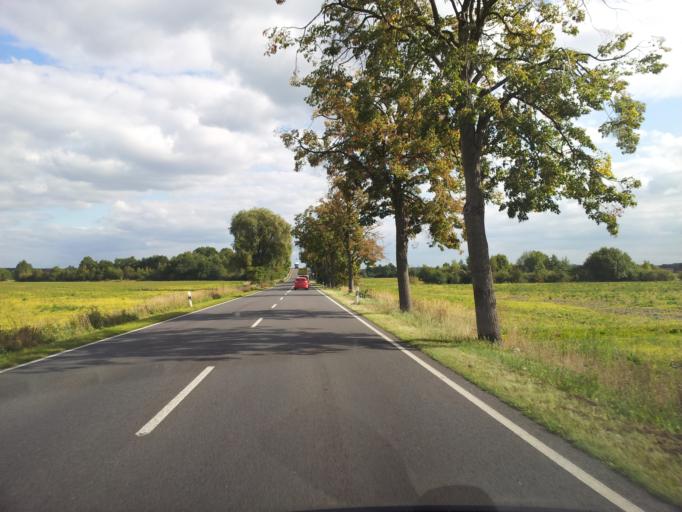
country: DE
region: Brandenburg
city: Grossraschen
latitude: 51.5899
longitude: 13.9337
